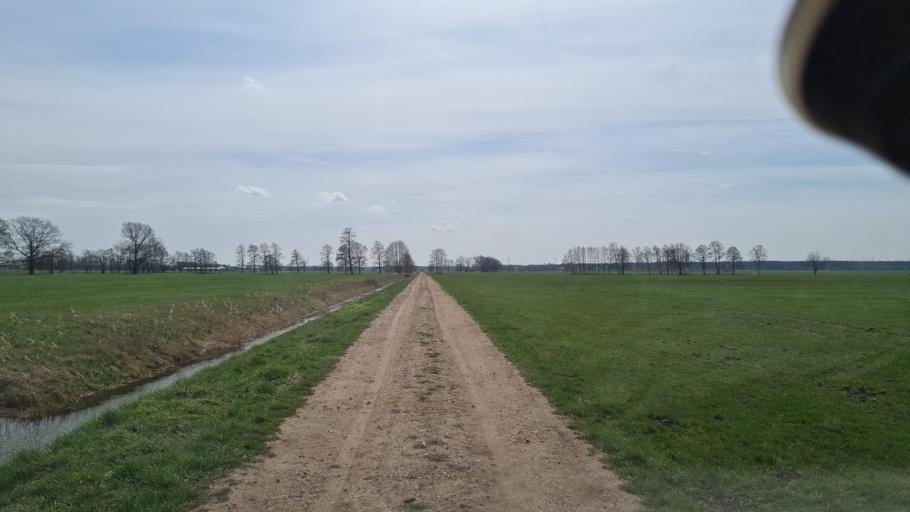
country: DE
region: Brandenburg
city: Bronkow
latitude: 51.6098
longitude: 13.9265
